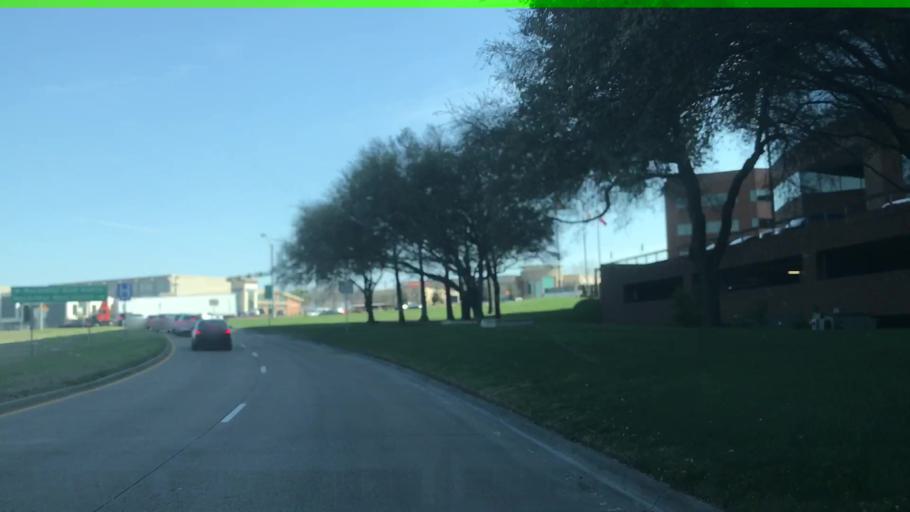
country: US
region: Texas
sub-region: Dallas County
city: Irving
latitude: 32.8895
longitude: -96.9648
